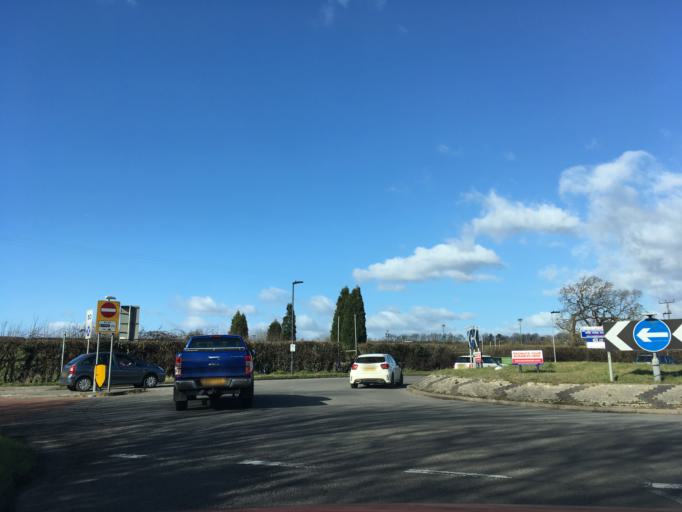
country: GB
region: England
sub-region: South Gloucestershire
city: Severn Beach
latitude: 51.5179
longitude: -2.6227
